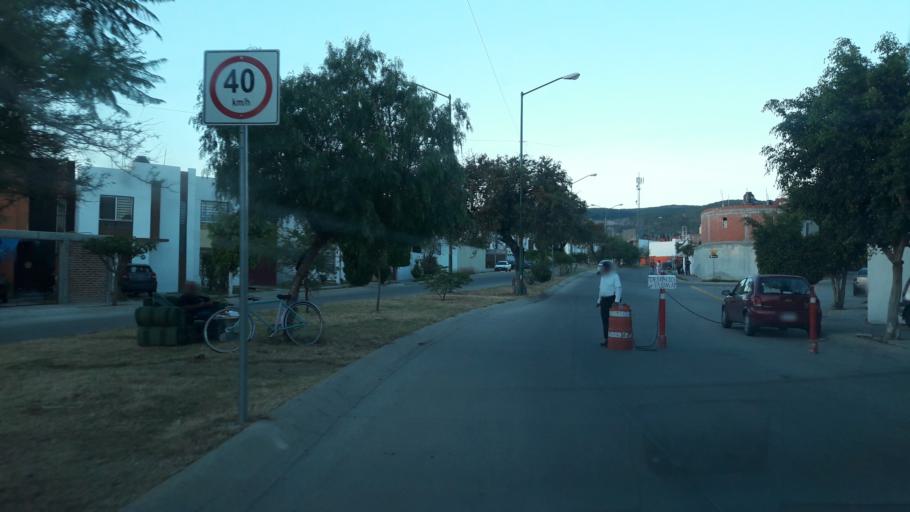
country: MX
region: Guanajuato
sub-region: Leon
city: Medina
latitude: 21.1650
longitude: -101.6322
